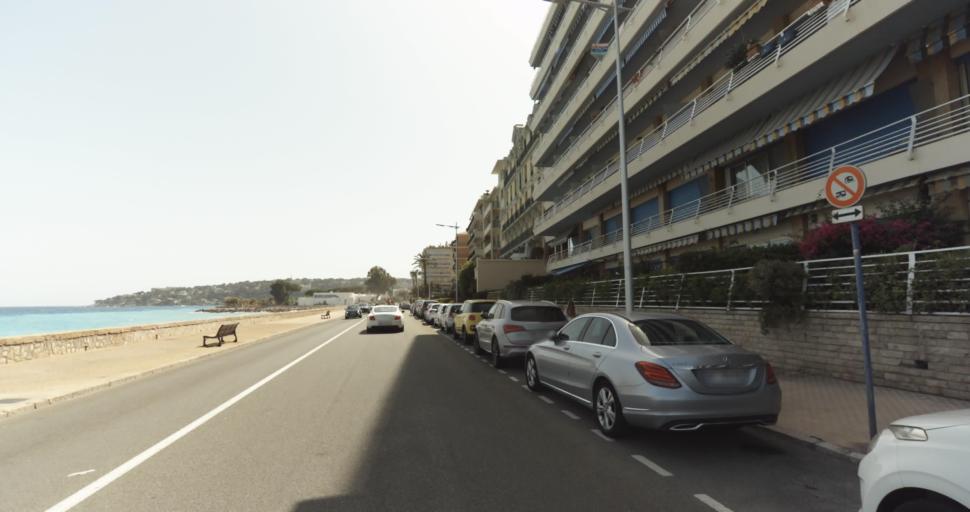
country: FR
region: Provence-Alpes-Cote d'Azur
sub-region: Departement des Alpes-Maritimes
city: Roquebrune-Cap-Martin
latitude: 43.7670
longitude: 7.4896
